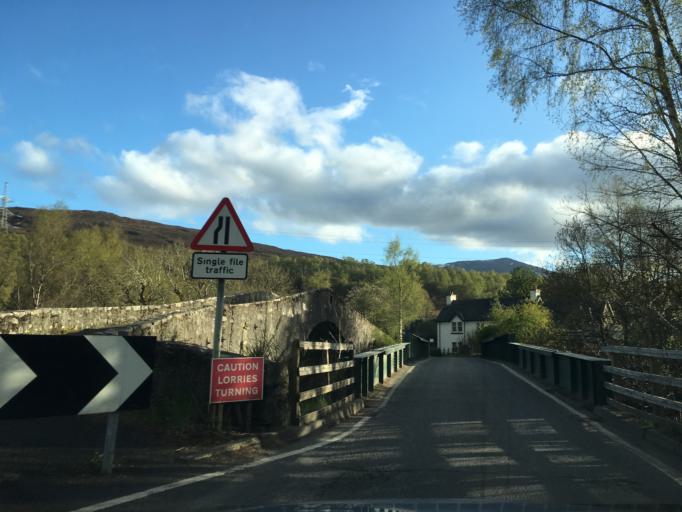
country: GB
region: Scotland
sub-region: Perth and Kinross
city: Aberfeldy
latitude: 56.7082
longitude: -4.0228
